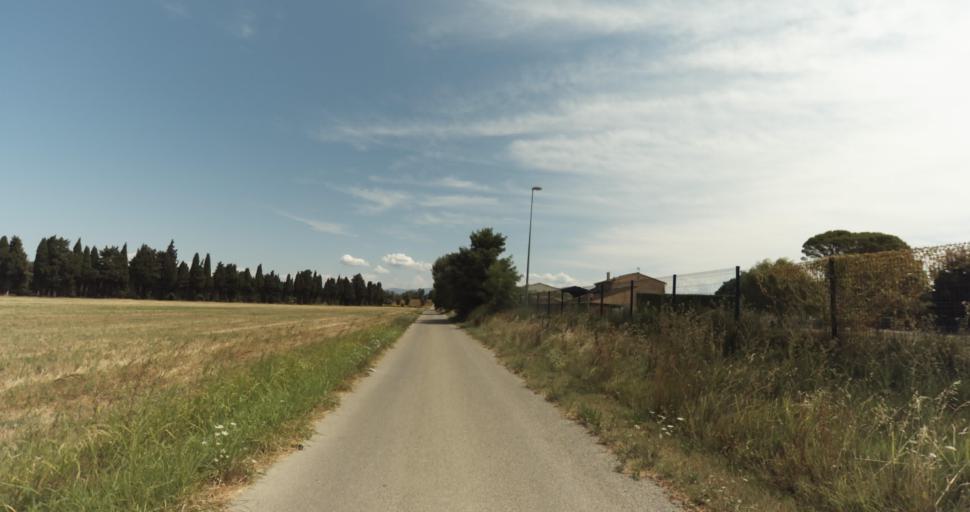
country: FR
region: Provence-Alpes-Cote d'Azur
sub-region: Departement du Vaucluse
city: Althen-des-Paluds
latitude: 44.0261
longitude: 4.9628
